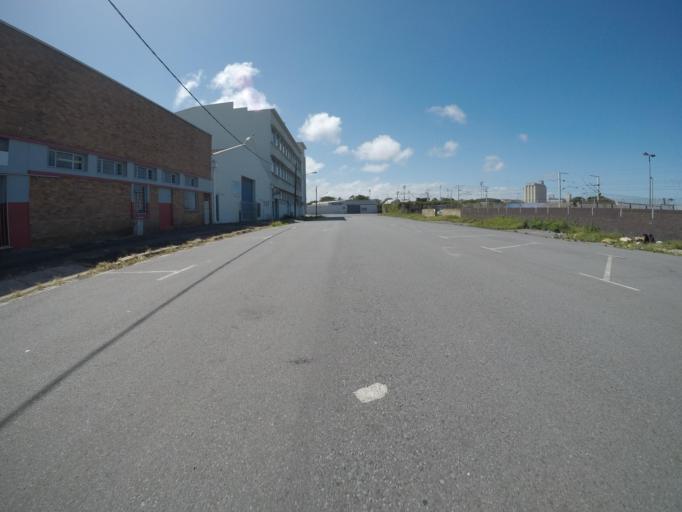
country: ZA
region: Eastern Cape
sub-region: Buffalo City Metropolitan Municipality
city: East London
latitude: -33.0140
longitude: 27.9061
